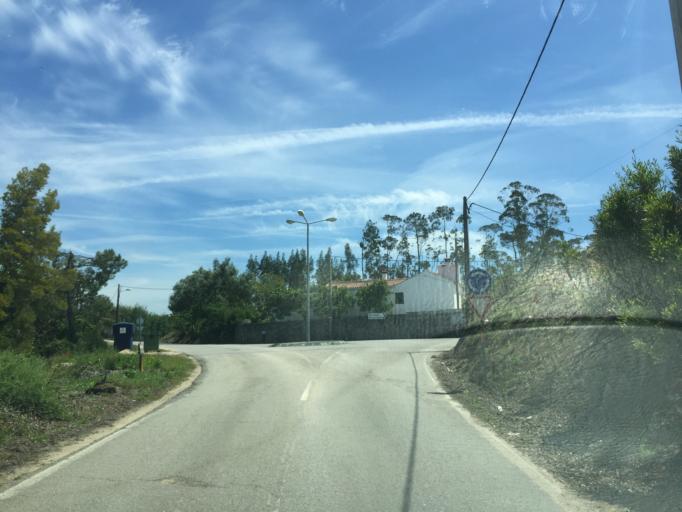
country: PT
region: Leiria
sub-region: Pombal
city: Lourical
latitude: 40.0643
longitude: -8.7142
